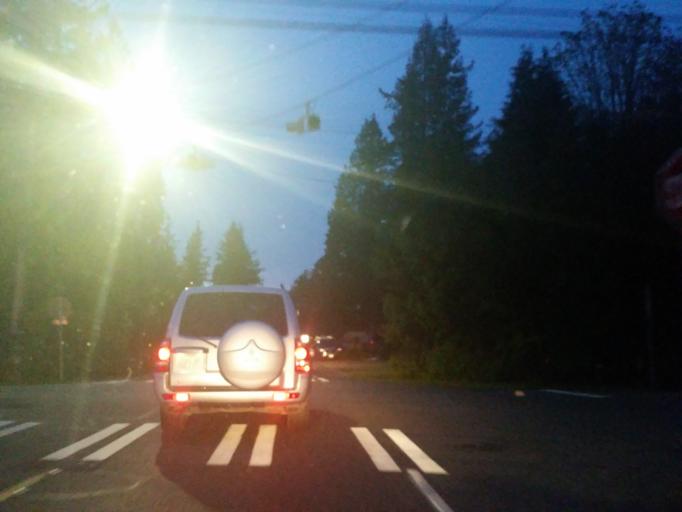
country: US
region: Washington
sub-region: Snohomish County
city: Esperance
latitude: 47.7704
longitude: -122.3611
